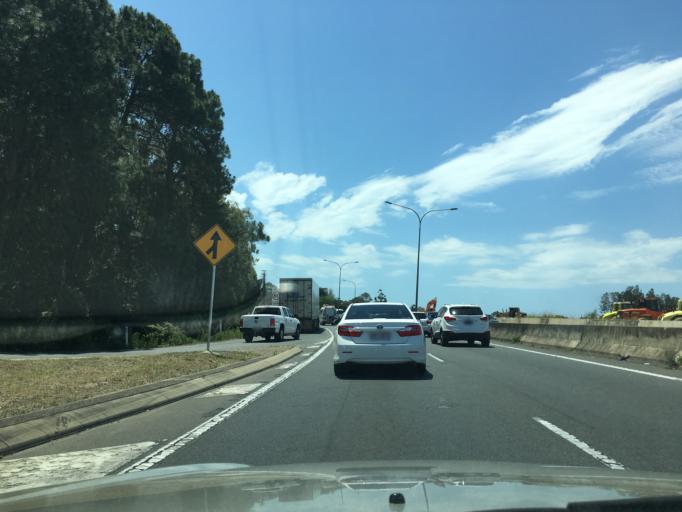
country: AU
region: Queensland
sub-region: Brisbane
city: Shorncliffe
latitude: -27.3768
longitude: 153.0957
